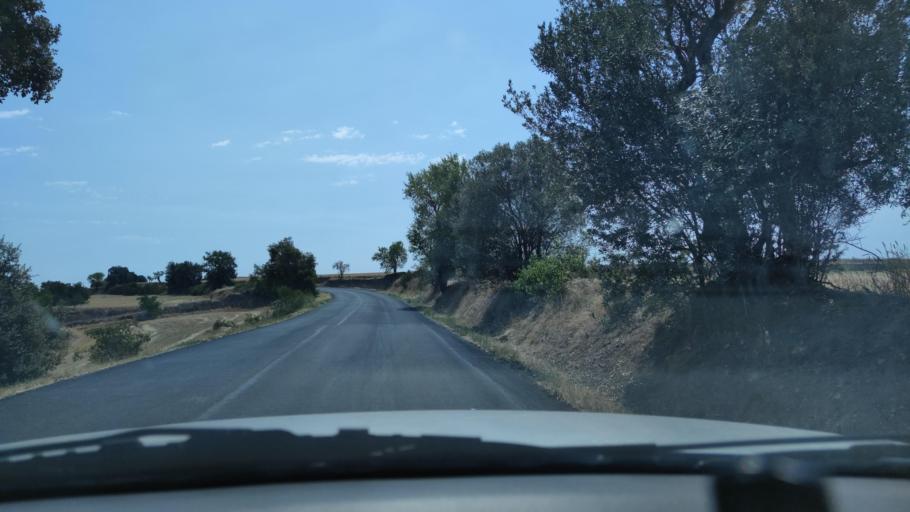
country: ES
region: Catalonia
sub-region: Provincia de Lleida
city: Ivorra
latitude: 41.7775
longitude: 1.3165
